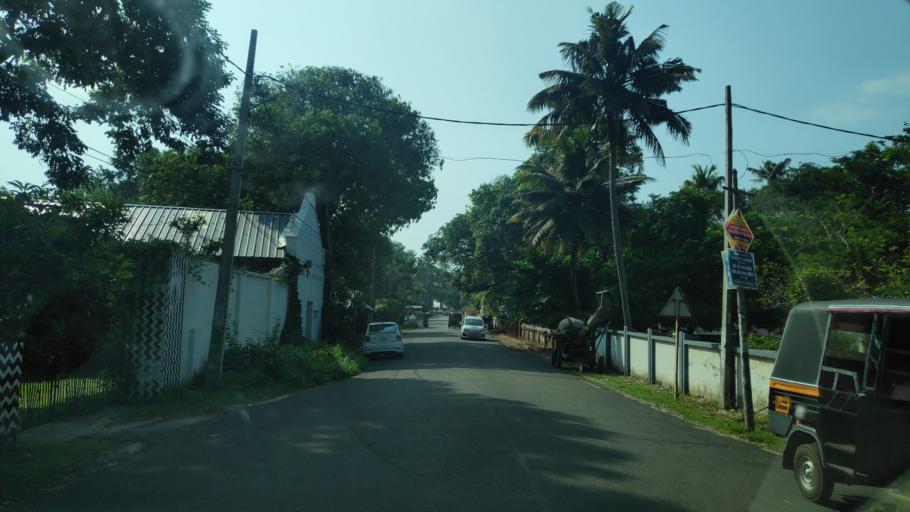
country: IN
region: Kerala
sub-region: Alappuzha
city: Alleppey
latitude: 9.4974
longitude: 76.3214
